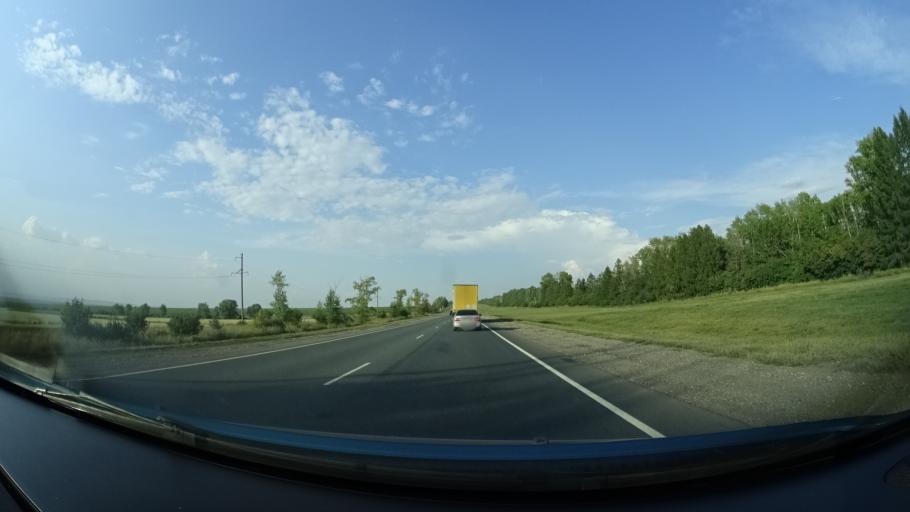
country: RU
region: Samara
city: Krasnyy Yar
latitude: 53.6556
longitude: 50.7480
